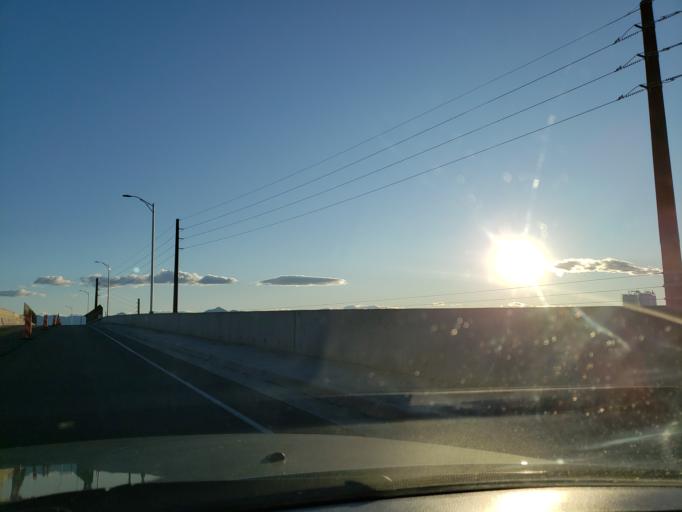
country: US
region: Arizona
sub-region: Maricopa County
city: Tolleson
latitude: 33.4455
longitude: -112.1871
